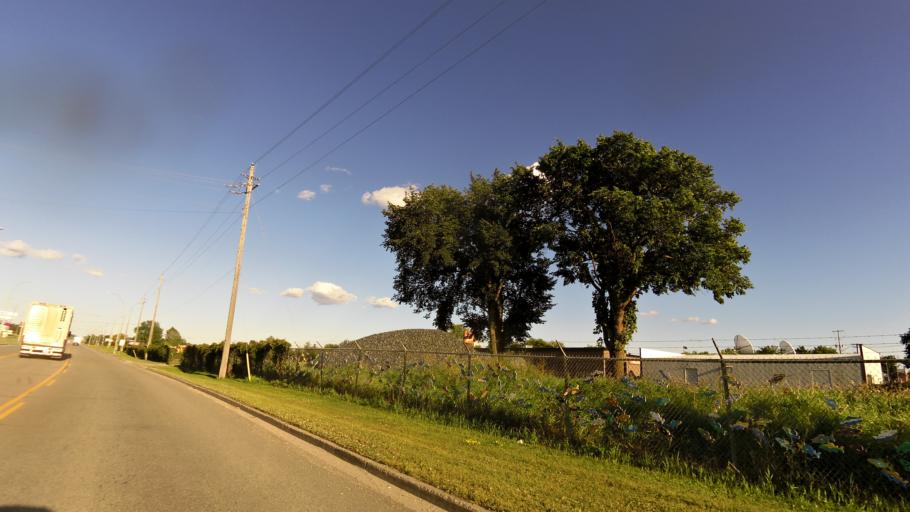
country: CA
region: Ontario
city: Dryden
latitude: 49.7862
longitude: -92.8366
